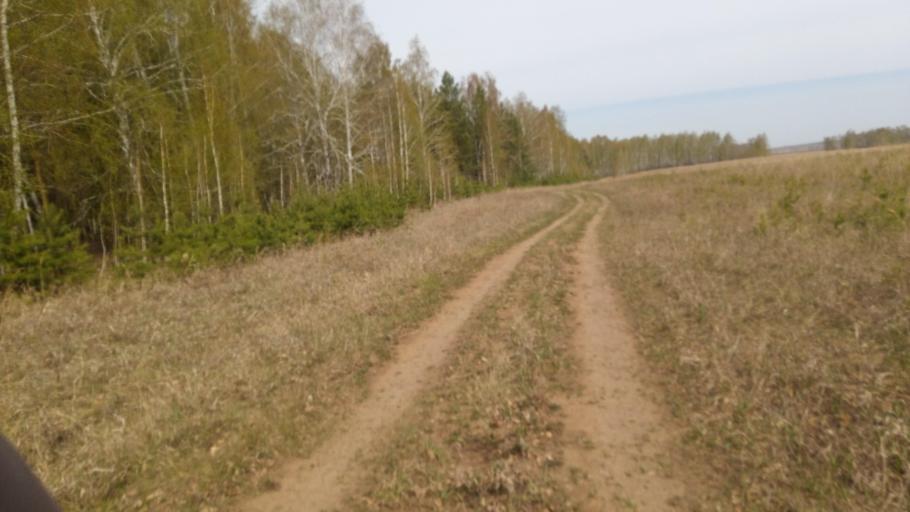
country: RU
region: Chelyabinsk
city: Timiryazevskiy
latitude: 55.0189
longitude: 60.8600
